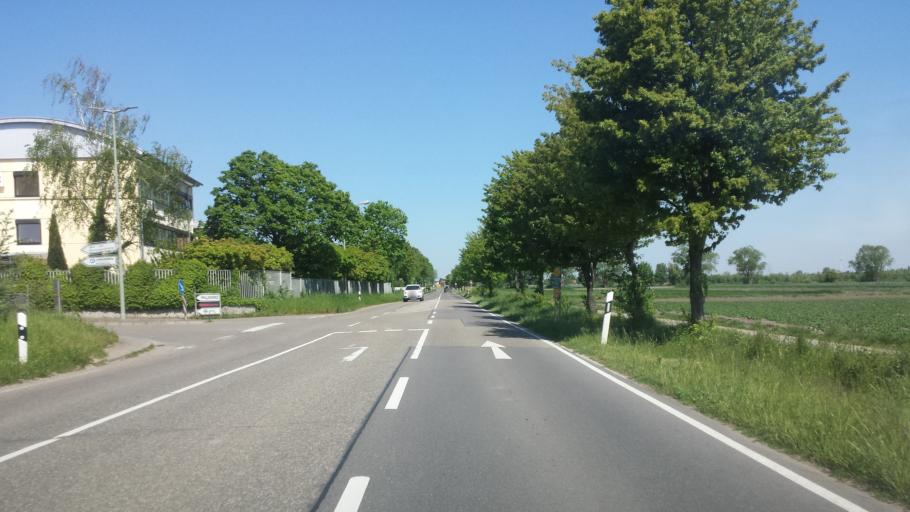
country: DE
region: Rheinland-Pfalz
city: Maxdorf
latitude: 49.4909
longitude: 8.2946
